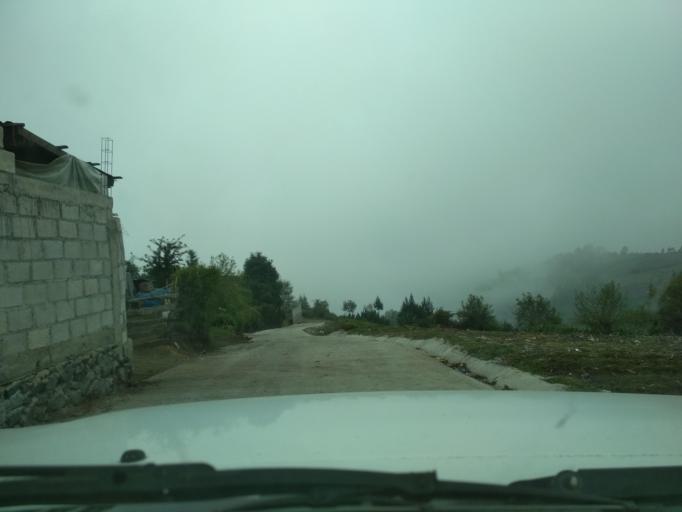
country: MX
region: Veracruz
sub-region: Mariano Escobedo
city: San Isidro el Berro
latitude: 18.9743
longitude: -97.2046
